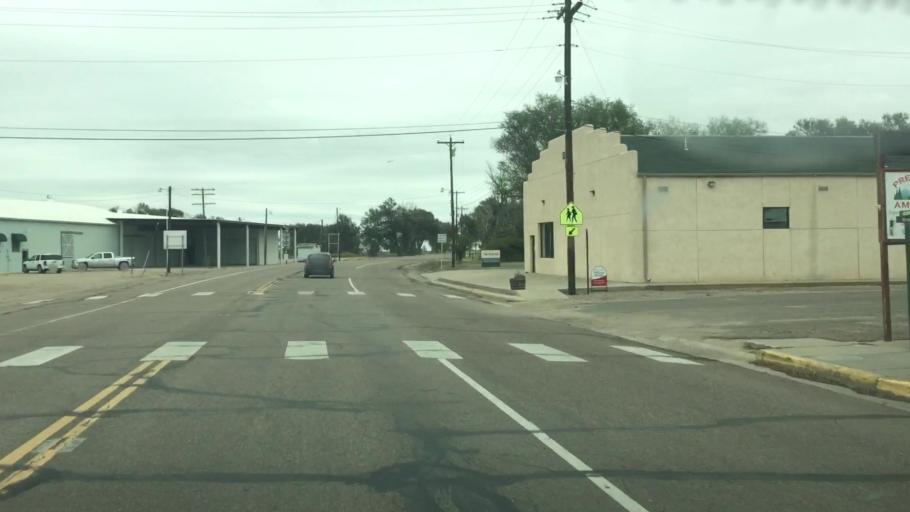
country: US
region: Colorado
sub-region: Prowers County
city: Lamar
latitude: 38.0627
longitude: -102.3093
